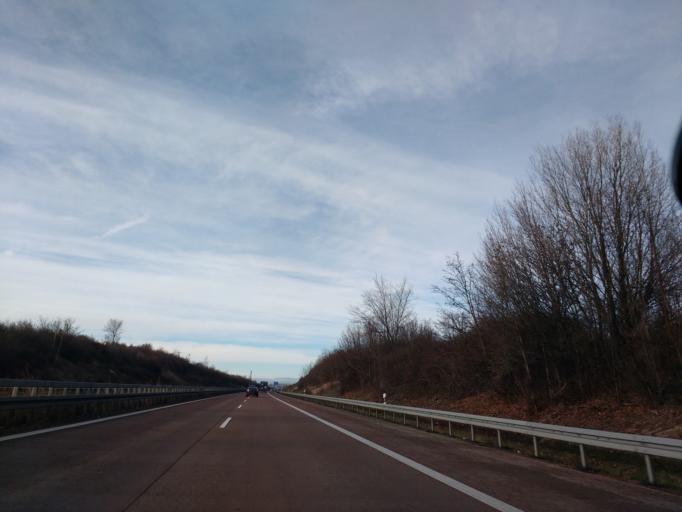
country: DE
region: Saxony-Anhalt
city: Wallwitz
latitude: 51.5691
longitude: 11.9301
